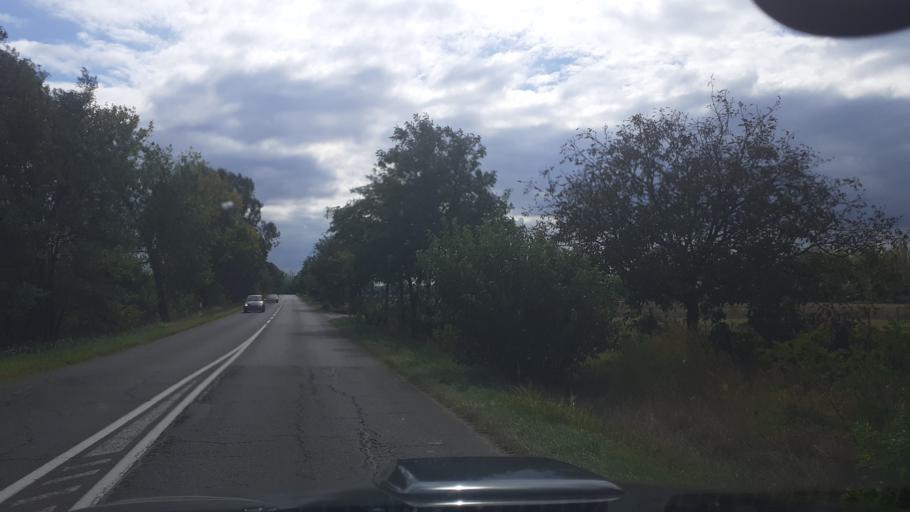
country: HU
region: Bacs-Kiskun
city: Apostag
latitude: 46.8836
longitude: 18.9773
